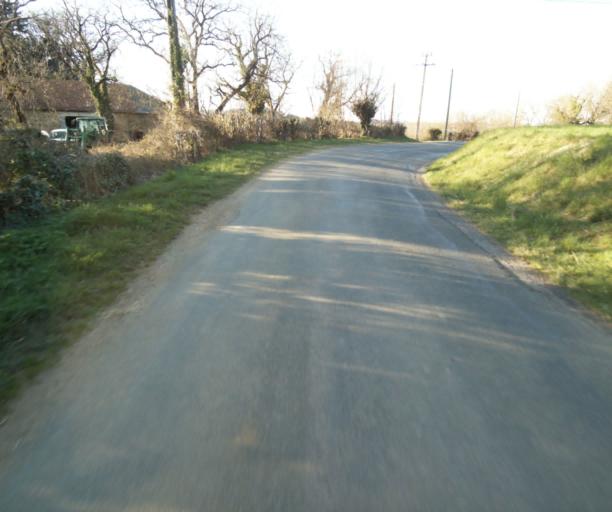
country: FR
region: Limousin
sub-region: Departement de la Correze
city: Seilhac
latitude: 45.3587
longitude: 1.7038
